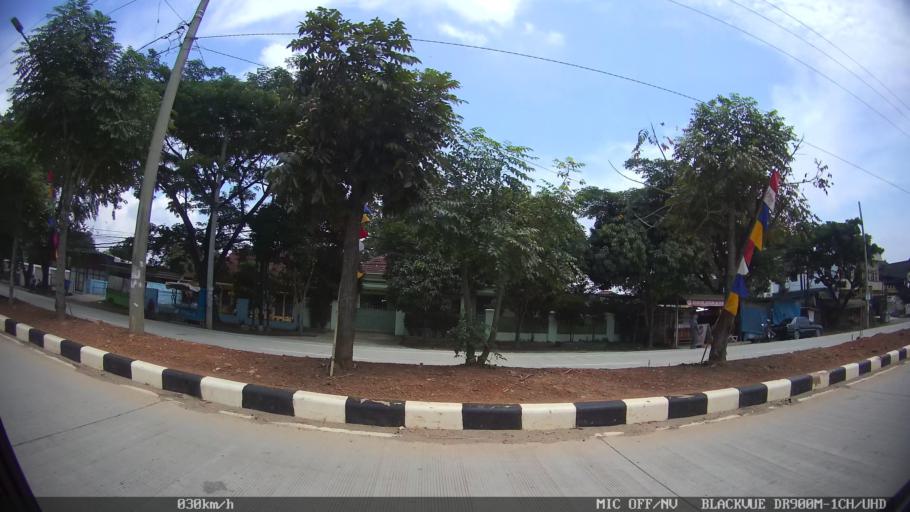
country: ID
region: Lampung
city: Kedaton
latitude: -5.3638
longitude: 105.3025
